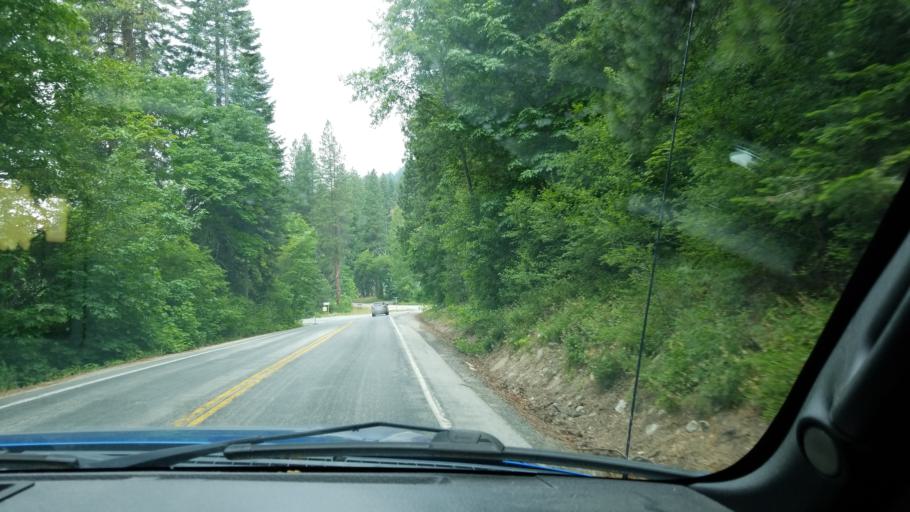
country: US
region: Washington
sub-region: Chelan County
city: Leavenworth
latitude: 47.8498
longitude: -120.8309
